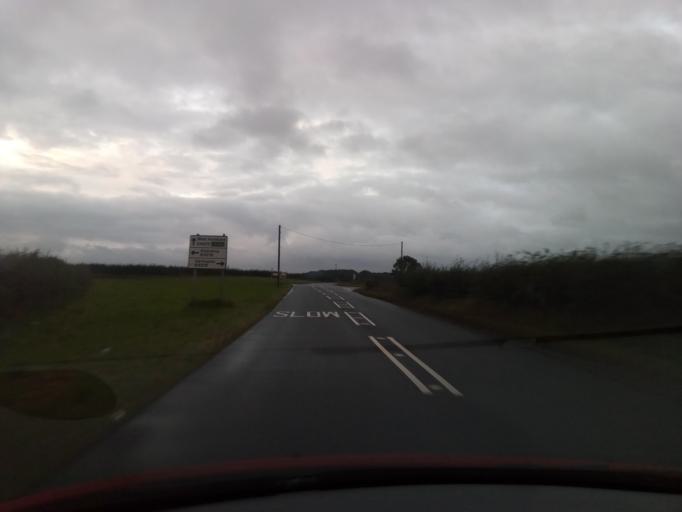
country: GB
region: England
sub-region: Darlington
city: Denton
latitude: 54.5633
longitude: -1.6765
